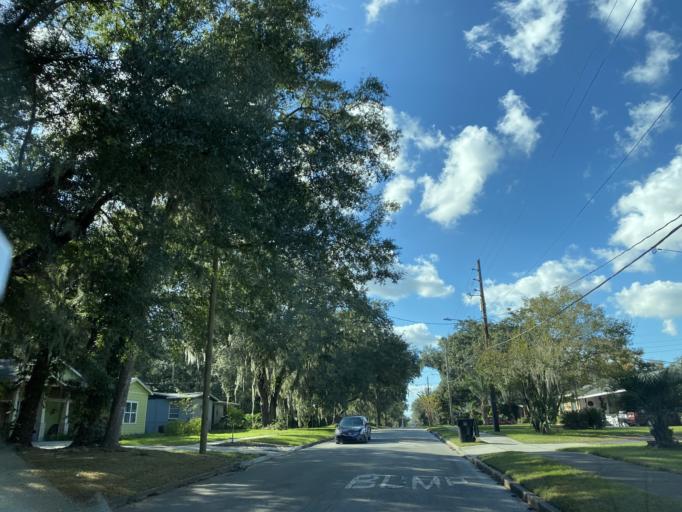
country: US
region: Florida
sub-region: Orange County
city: Orlando
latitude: 28.5519
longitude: -81.4027
